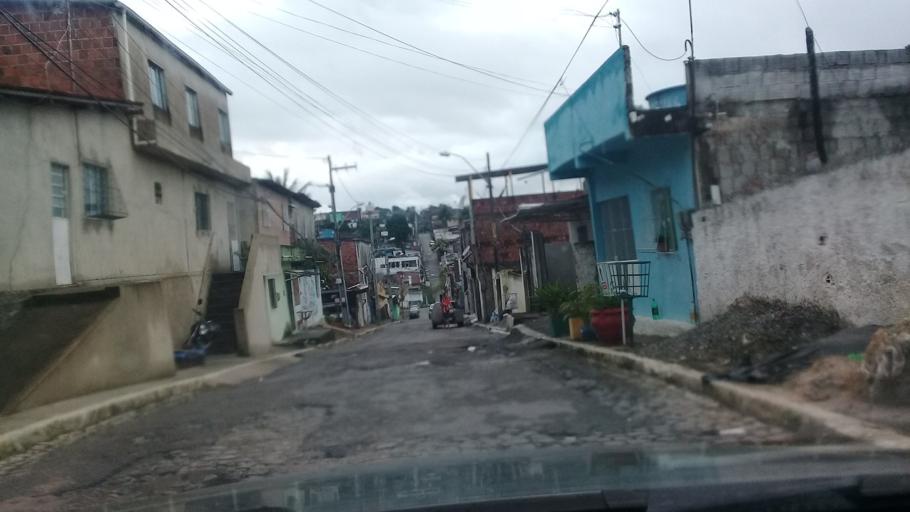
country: BR
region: Pernambuco
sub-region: Jaboatao Dos Guararapes
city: Jaboatao dos Guararapes
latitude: -8.1303
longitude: -34.9468
